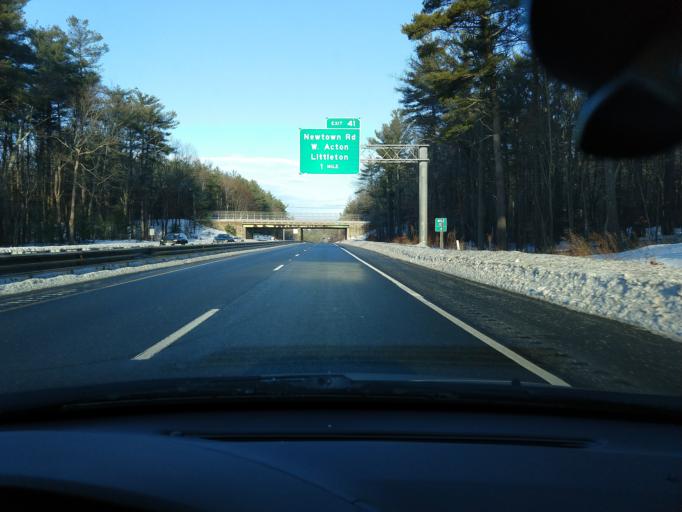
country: US
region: Massachusetts
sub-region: Middlesex County
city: Acton
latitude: 42.4900
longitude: -71.4585
